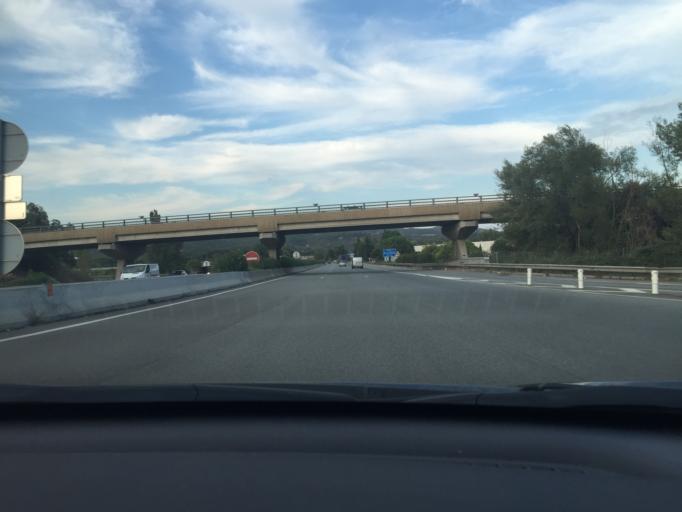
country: FR
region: Provence-Alpes-Cote d'Azur
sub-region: Departement du Var
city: Frejus
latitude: 43.4696
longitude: 6.7319
